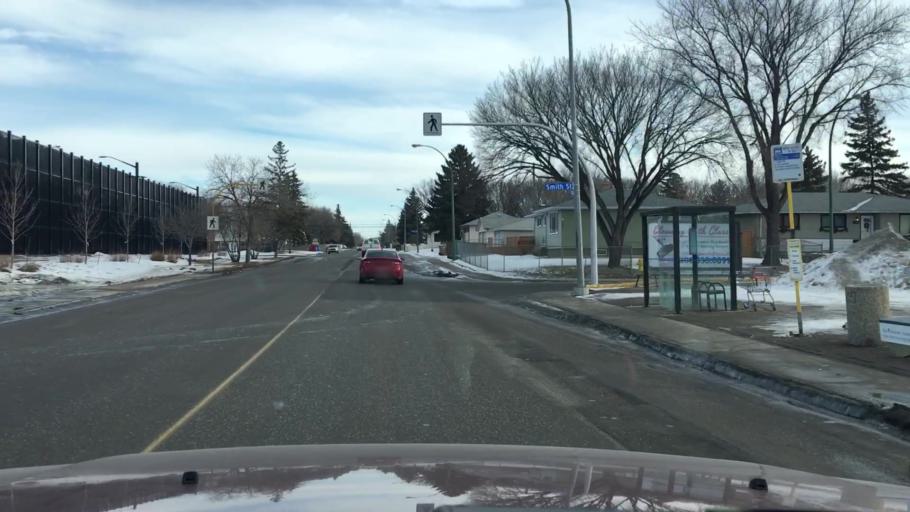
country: CA
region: Saskatchewan
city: Regina
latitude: 50.4808
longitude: -104.6157
